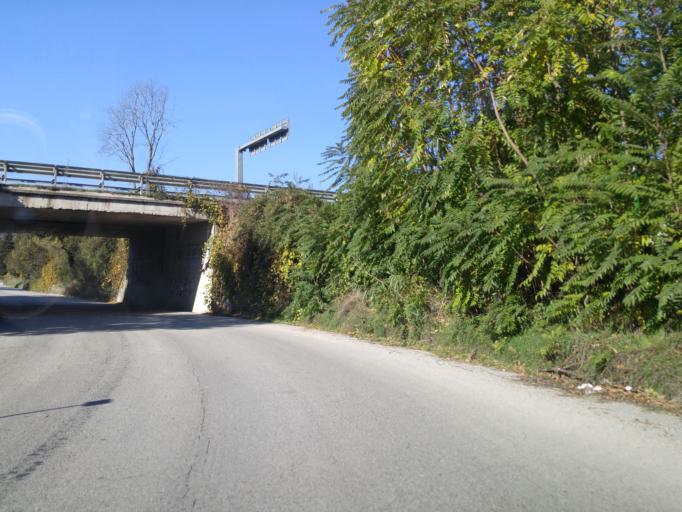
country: IT
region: The Marches
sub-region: Provincia di Pesaro e Urbino
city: Tavernelle
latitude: 43.7259
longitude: 12.8930
